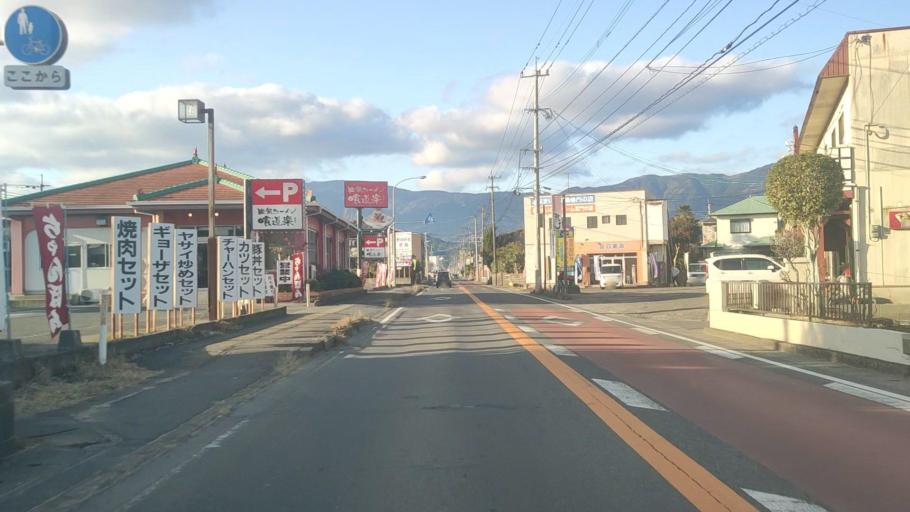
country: JP
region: Saga Prefecture
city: Saga-shi
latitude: 33.2817
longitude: 130.2115
